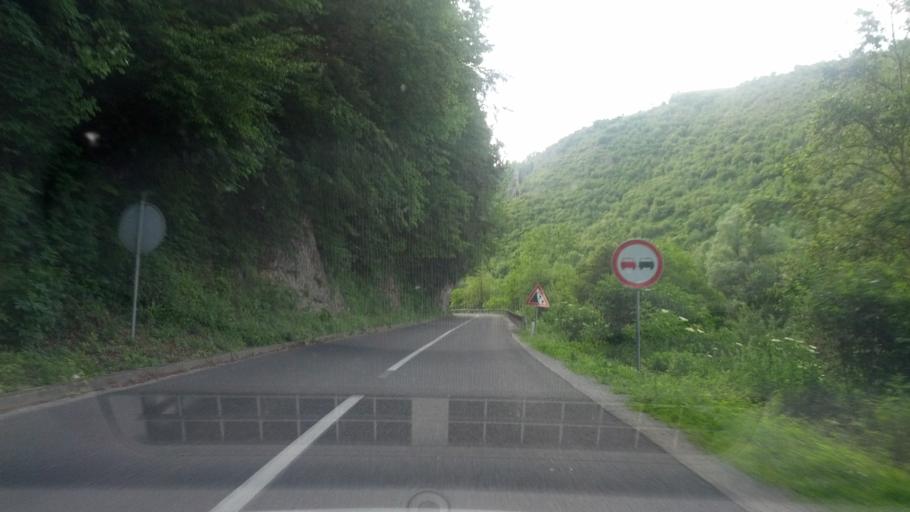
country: BA
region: Federation of Bosnia and Herzegovina
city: Ostrozac
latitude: 44.9090
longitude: 15.9758
